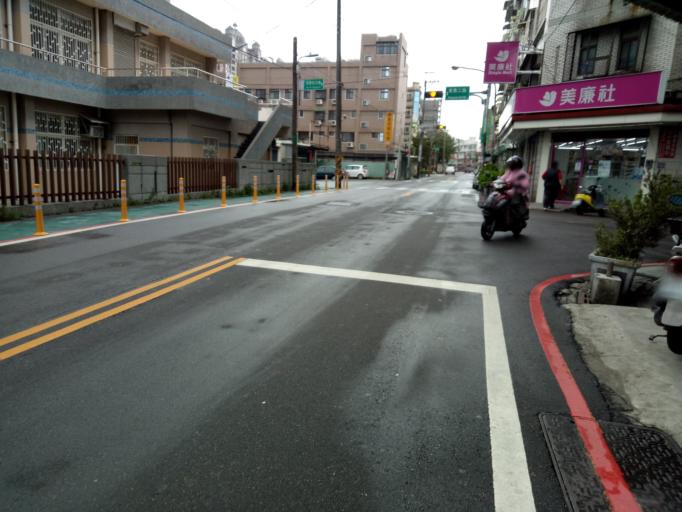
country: TW
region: Taiwan
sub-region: Taoyuan
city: Taoyuan
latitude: 24.9678
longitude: 121.3034
